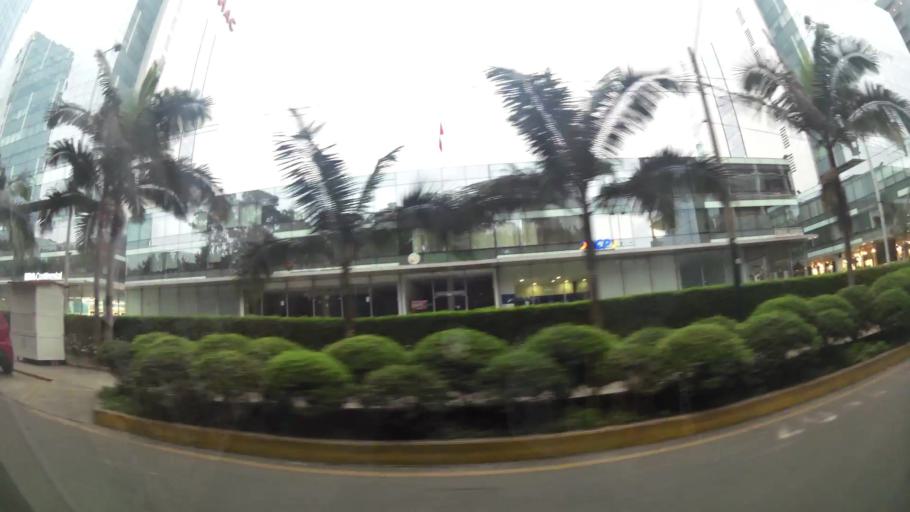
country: PE
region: Lima
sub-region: Lima
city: San Luis
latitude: -12.0932
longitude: -77.0247
